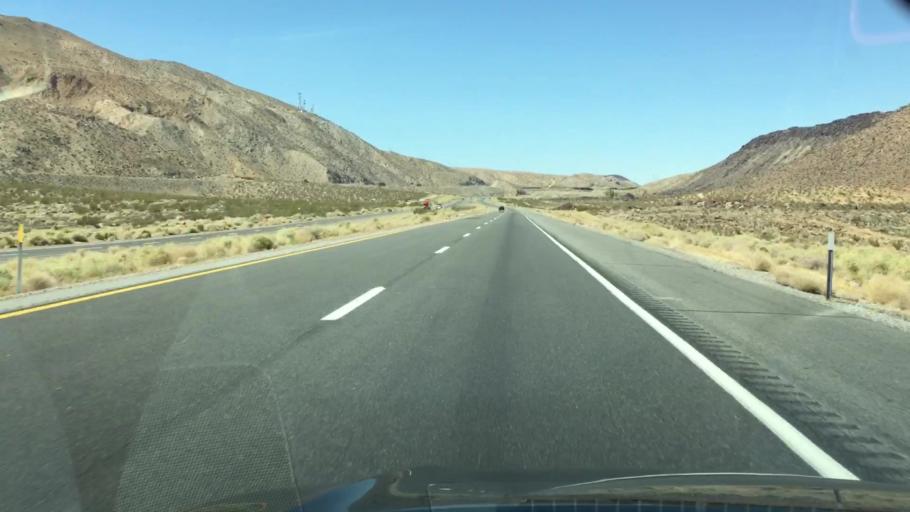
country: US
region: California
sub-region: Kern County
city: Inyokern
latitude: 35.9102
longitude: -117.9029
